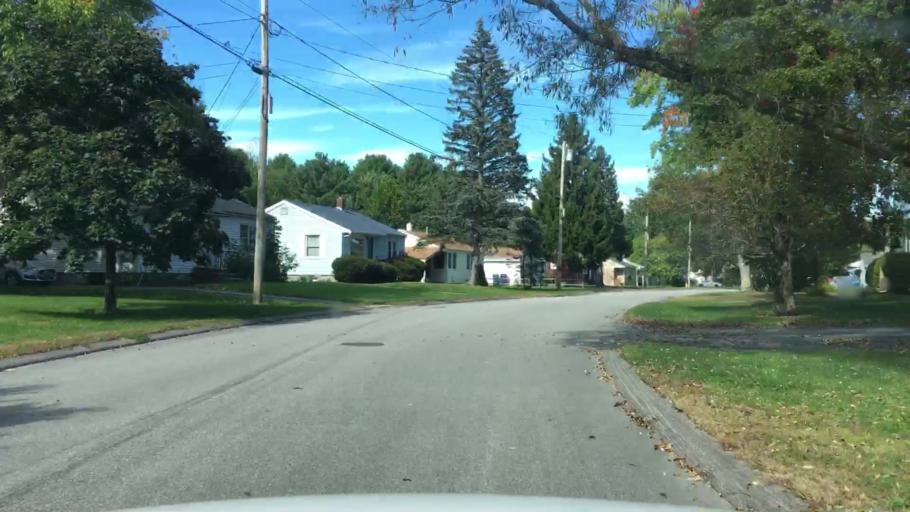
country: US
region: Maine
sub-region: Cumberland County
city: Westbrook
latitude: 43.6746
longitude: -70.3849
